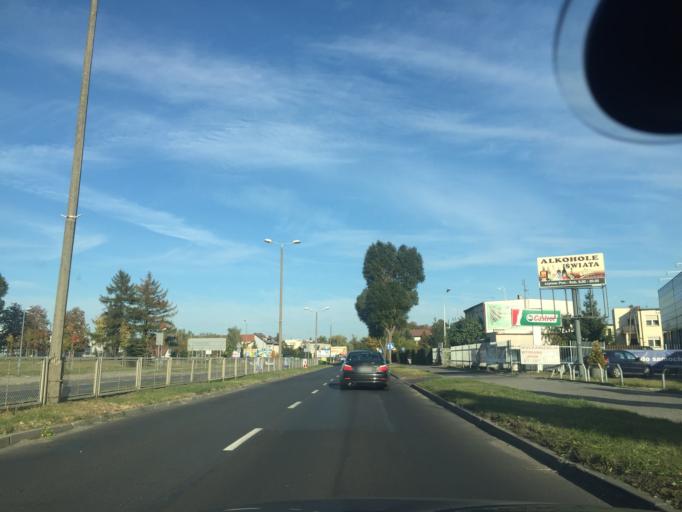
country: PL
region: Kujawsko-Pomorskie
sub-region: Powiat inowroclawski
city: Inowroclaw
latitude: 52.7885
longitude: 18.2627
